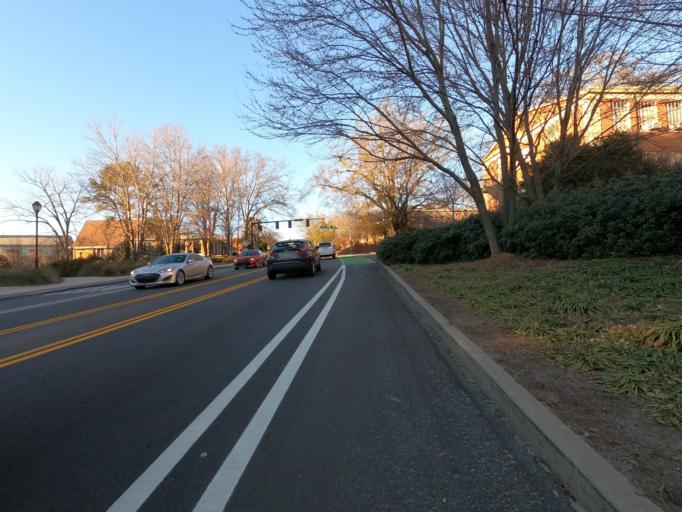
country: US
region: Georgia
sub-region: Clarke County
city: Athens
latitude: 33.9524
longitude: -83.3766
